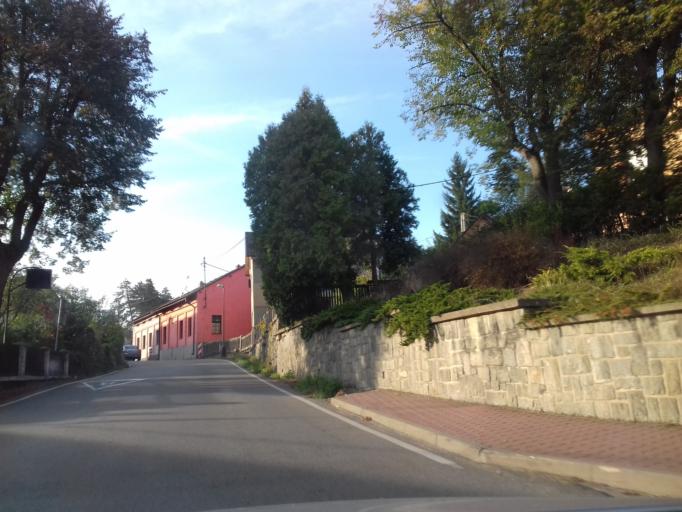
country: CZ
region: Central Bohemia
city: Kamenny Privoz
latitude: 49.8636
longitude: 14.5034
